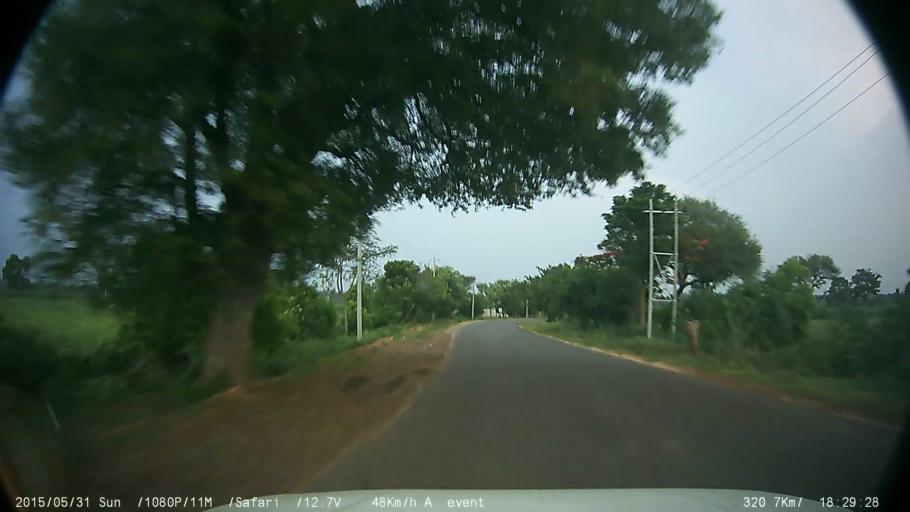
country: IN
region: Karnataka
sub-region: Mysore
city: Nanjangud
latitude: 12.1223
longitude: 76.7307
